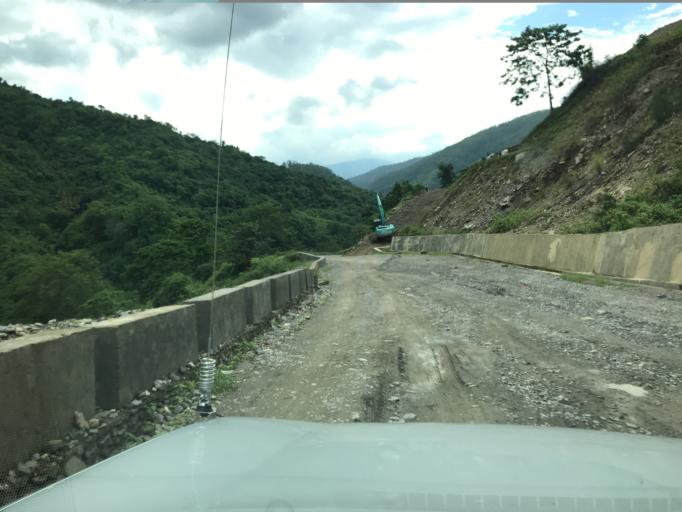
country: TL
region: Aileu
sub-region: Aileu Villa
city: Aileu
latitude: -8.6421
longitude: 125.5133
